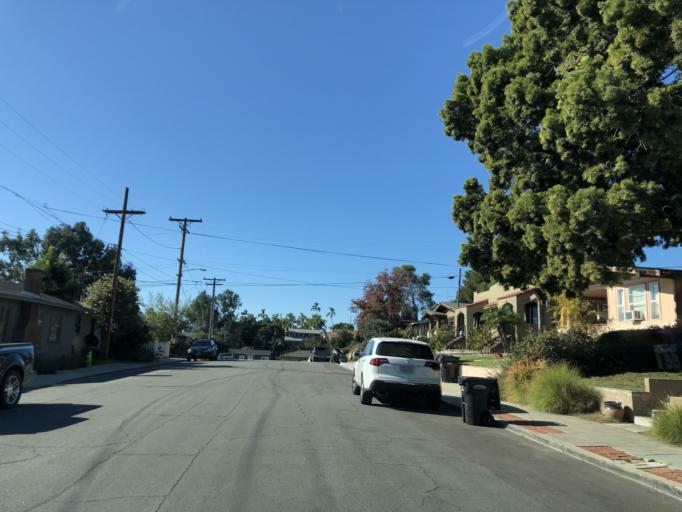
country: US
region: California
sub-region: San Diego County
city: San Diego
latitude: 32.7348
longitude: -117.1282
